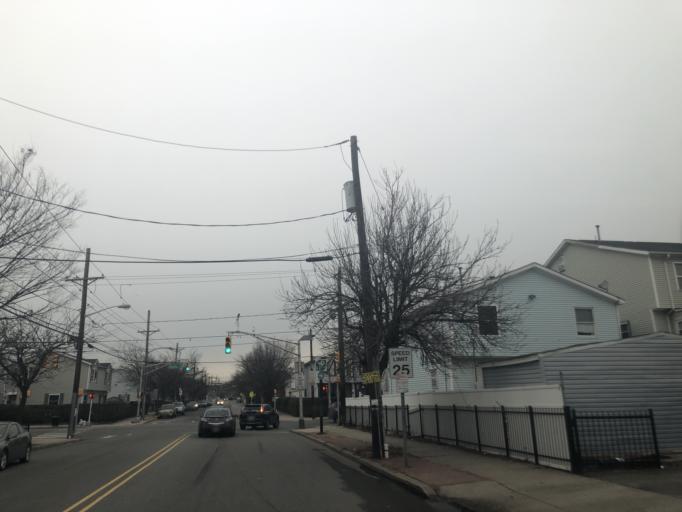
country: US
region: New Jersey
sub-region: Hudson County
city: Jersey City
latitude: 40.7134
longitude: -74.0583
